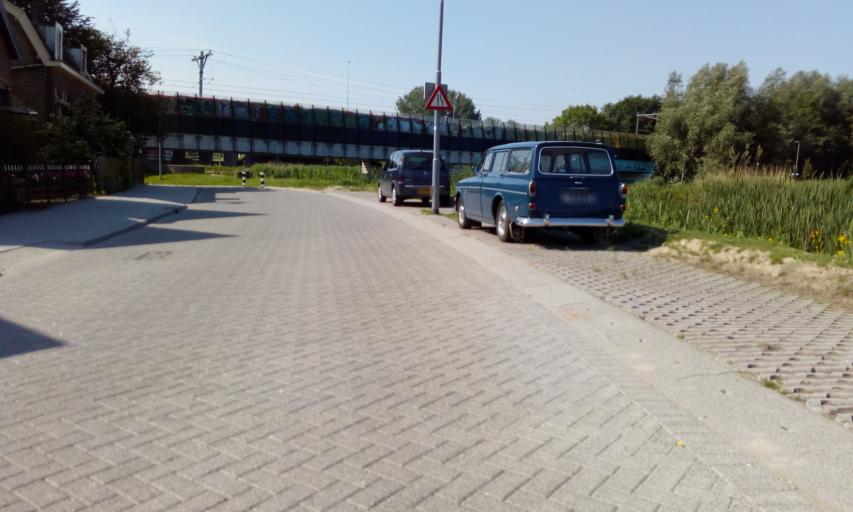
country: NL
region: South Holland
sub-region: Gemeente Rotterdam
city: Rotterdam
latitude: 51.9436
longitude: 4.4860
